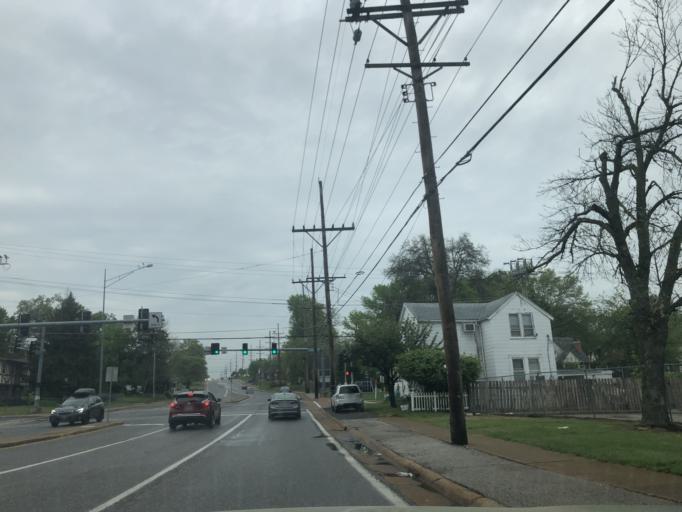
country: US
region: Missouri
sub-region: Saint Louis County
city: Affton
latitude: 38.5544
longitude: -90.3230
